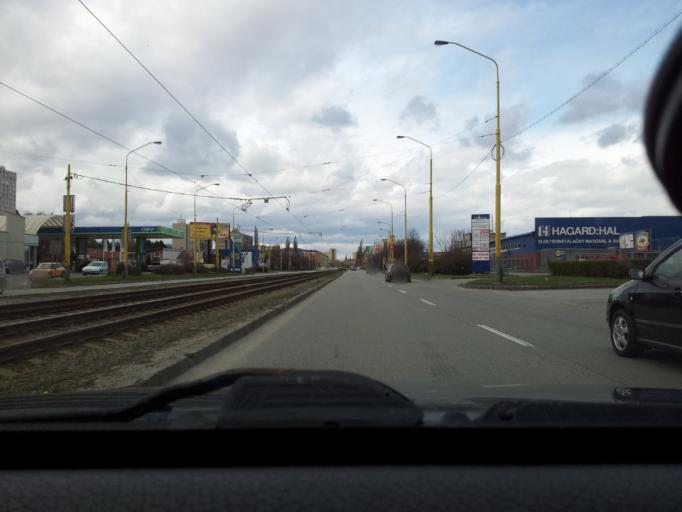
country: SK
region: Kosicky
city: Kosice
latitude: 48.6997
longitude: 21.2635
